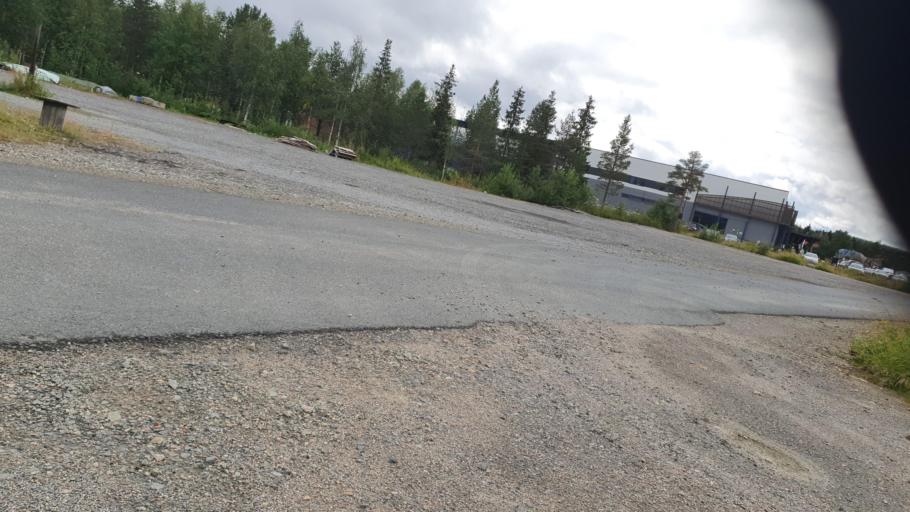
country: FI
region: Lapland
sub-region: Tunturi-Lappi
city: Kolari
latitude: 67.6066
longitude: 24.1557
